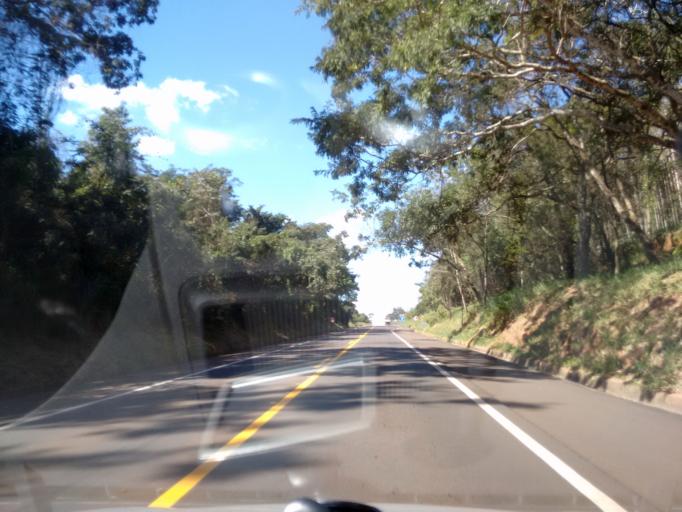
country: BR
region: Sao Paulo
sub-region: Ribeirao Bonito
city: Ribeirao Bonito
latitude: -22.0842
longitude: -48.1591
